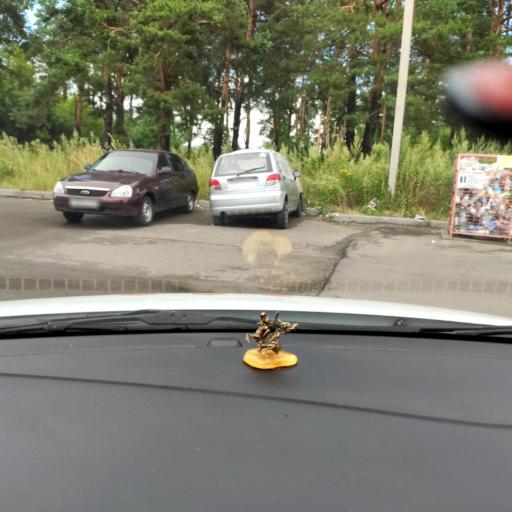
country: RU
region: Tatarstan
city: Stolbishchi
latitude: 55.6161
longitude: 49.1398
